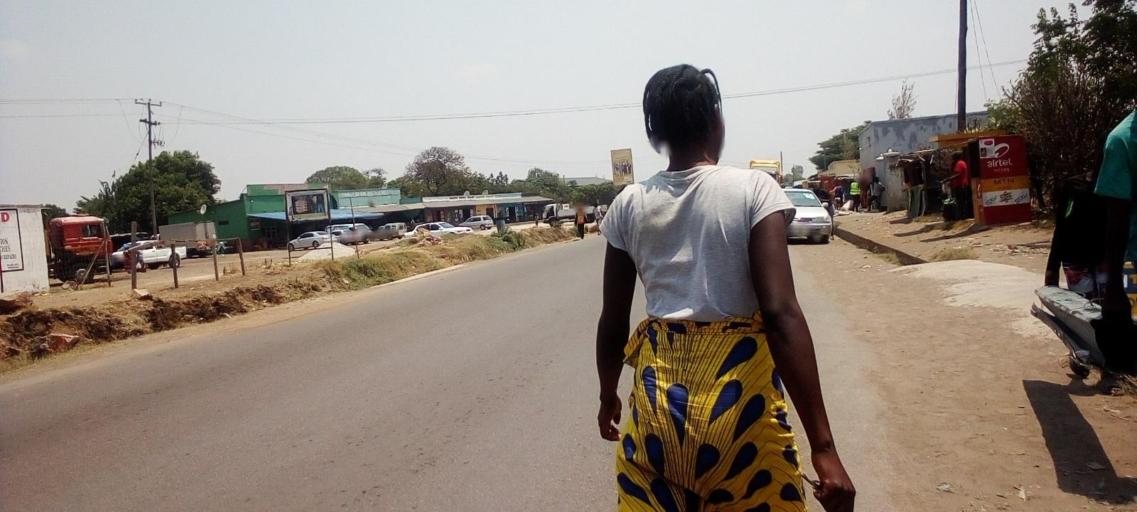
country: ZM
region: Lusaka
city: Lusaka
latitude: -15.4454
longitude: 28.2469
